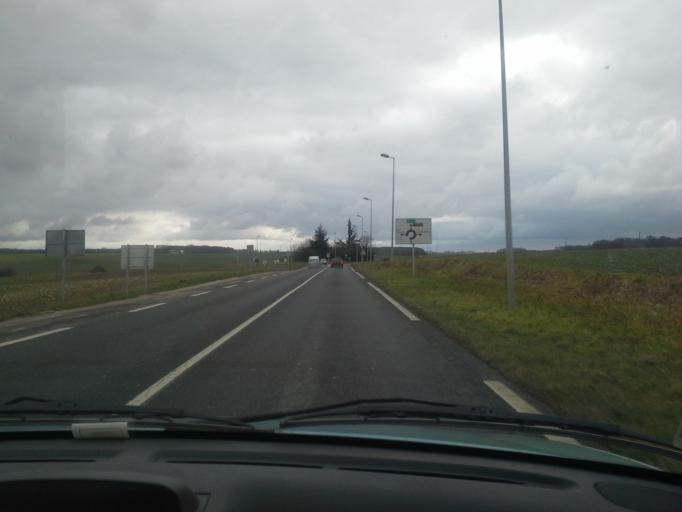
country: FR
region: Centre
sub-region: Departement du Loir-et-Cher
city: Vendome
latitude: 47.7761
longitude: 1.0808
